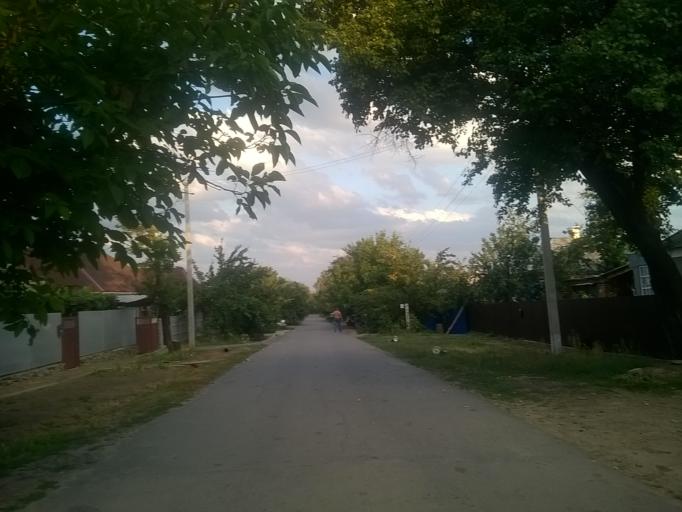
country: RU
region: Rostov
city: Donetsk
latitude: 48.3346
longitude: 39.9574
